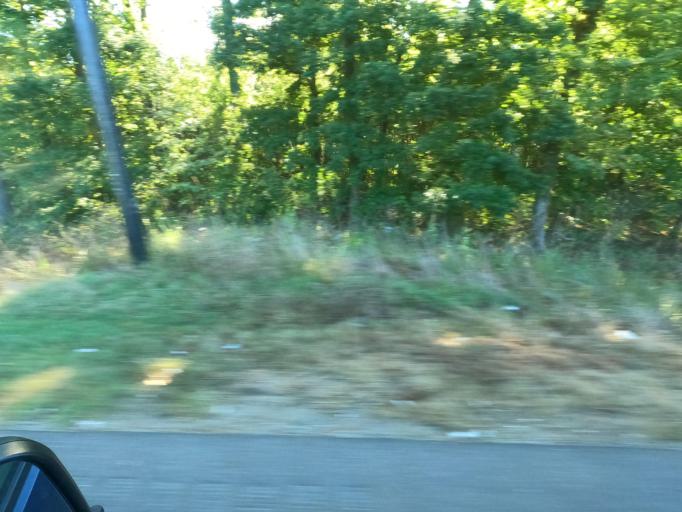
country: US
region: Tennessee
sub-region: Tipton County
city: Atoka
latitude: 35.4547
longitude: -89.7750
